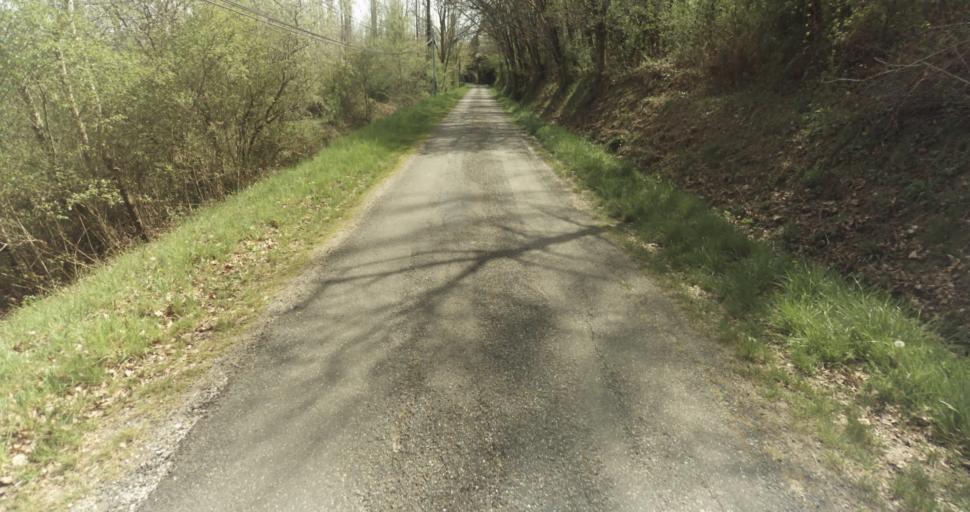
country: FR
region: Midi-Pyrenees
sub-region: Departement du Tarn-et-Garonne
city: Moissac
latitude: 44.1445
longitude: 1.0947
